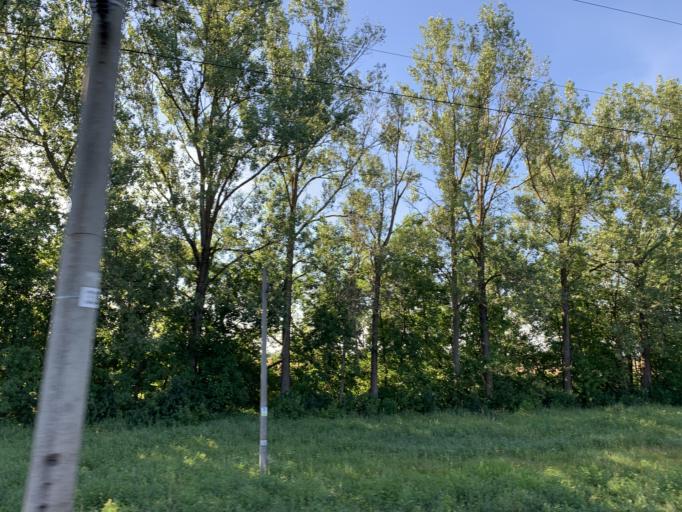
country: BY
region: Minsk
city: Novy Svyerzhan'
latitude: 53.4057
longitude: 26.6318
